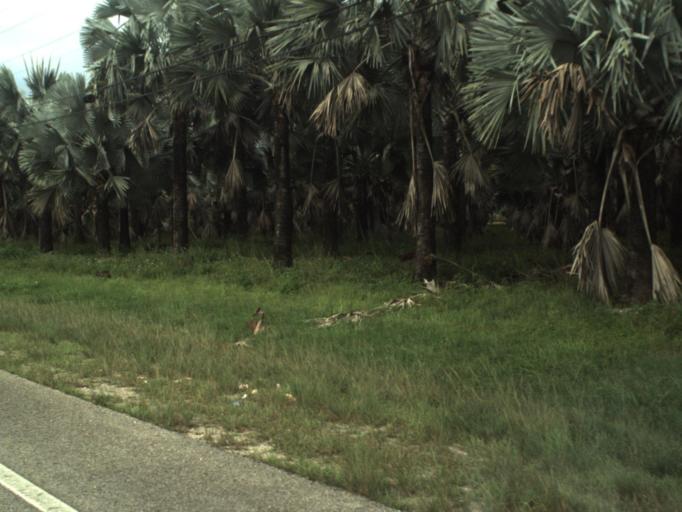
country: US
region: Florida
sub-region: Miami-Dade County
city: Homestead
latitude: 25.4998
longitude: -80.4777
